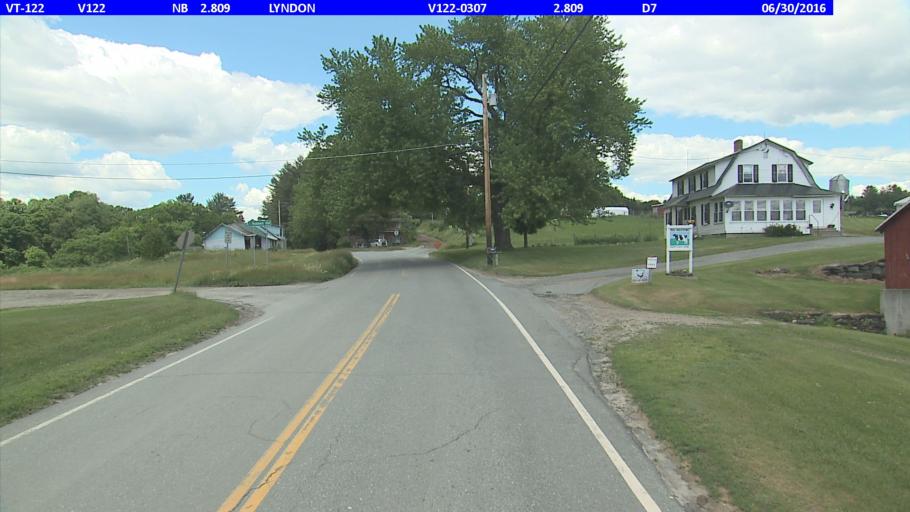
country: US
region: Vermont
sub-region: Caledonia County
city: Lyndonville
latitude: 44.5652
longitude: -72.0408
